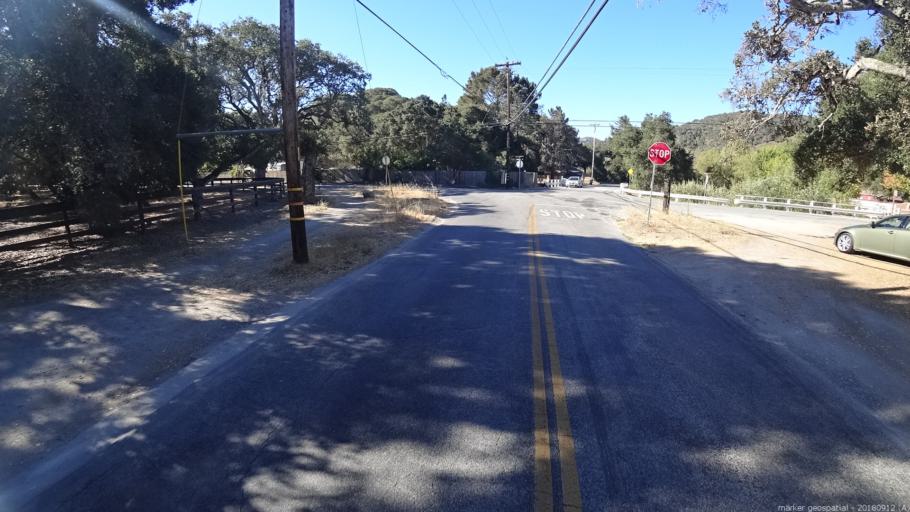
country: US
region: California
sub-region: Monterey County
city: Carmel Valley Village
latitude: 36.5500
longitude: -121.7325
